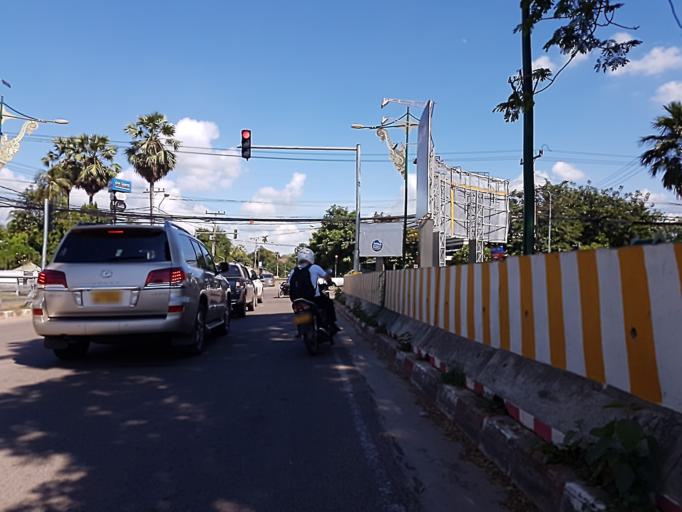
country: LA
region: Vientiane
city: Vientiane
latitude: 17.9396
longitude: 102.6176
